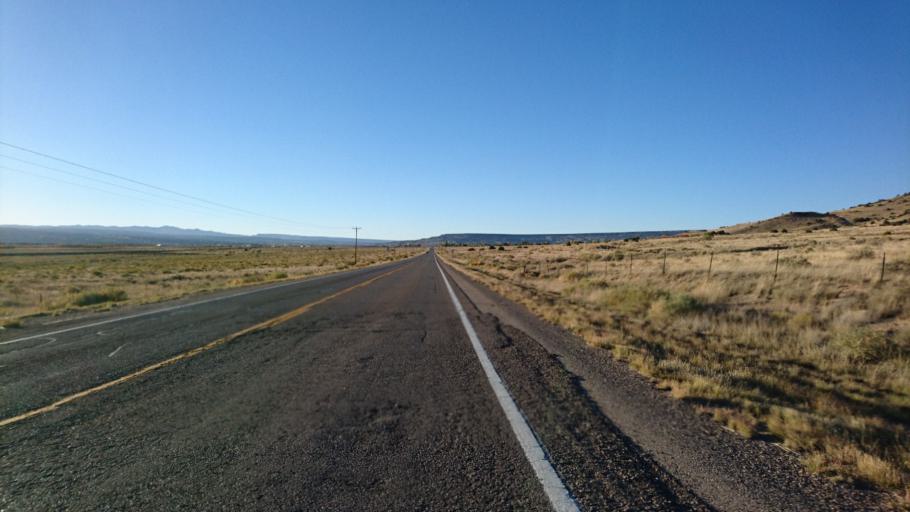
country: US
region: New Mexico
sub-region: Cibola County
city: Grants
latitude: 35.1180
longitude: -107.7904
